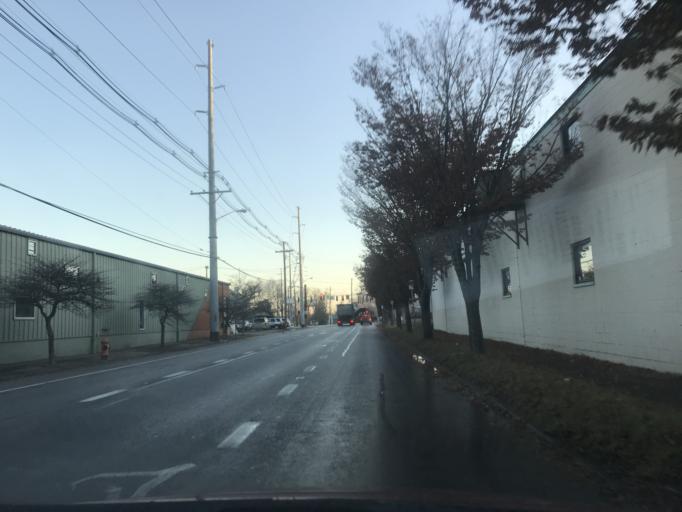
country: US
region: Indiana
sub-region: Clark County
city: Jeffersonville
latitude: 38.2593
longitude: -85.7177
